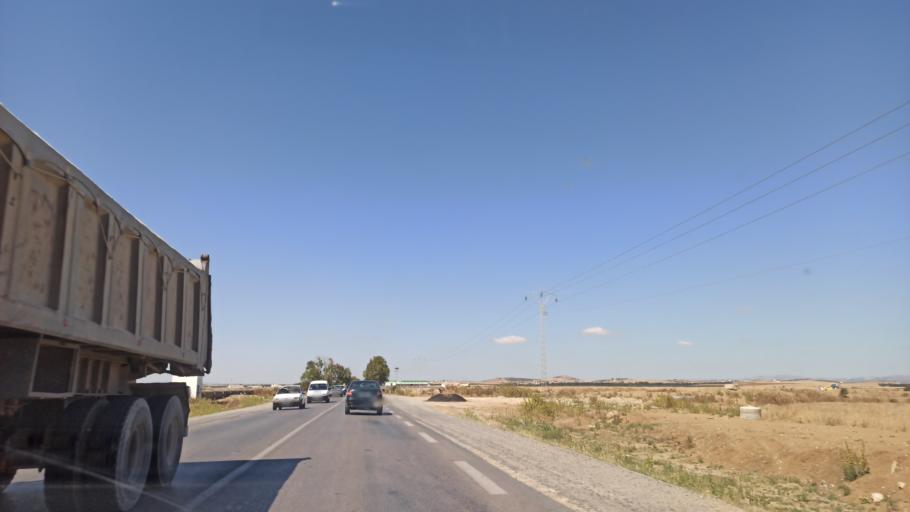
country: TN
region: Tunis
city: Oued Lill
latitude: 36.7445
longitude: 9.9621
